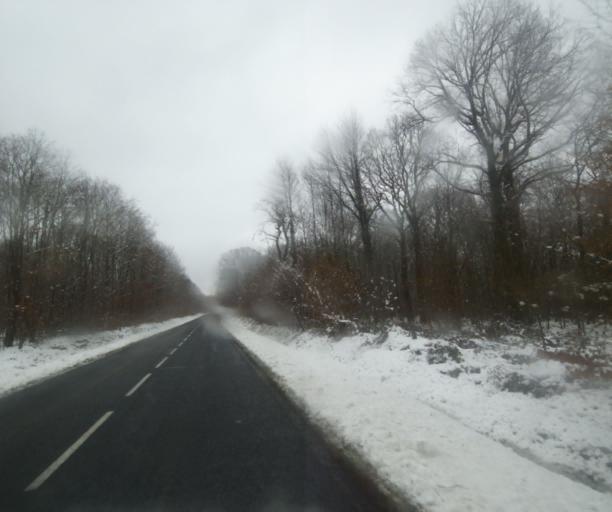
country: FR
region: Champagne-Ardenne
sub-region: Departement de la Haute-Marne
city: Laneuville-a-Remy
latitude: 48.4542
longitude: 4.8755
